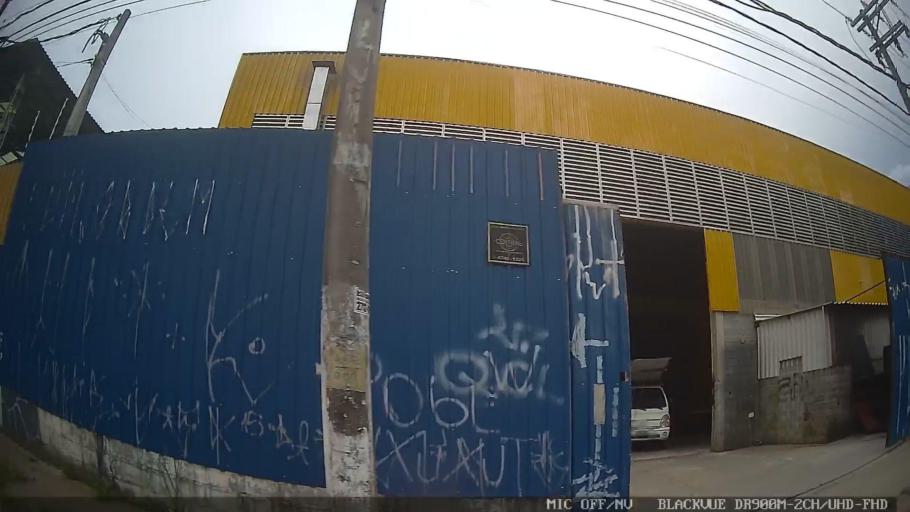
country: BR
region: Sao Paulo
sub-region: Suzano
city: Suzano
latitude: -23.5425
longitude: -46.2907
